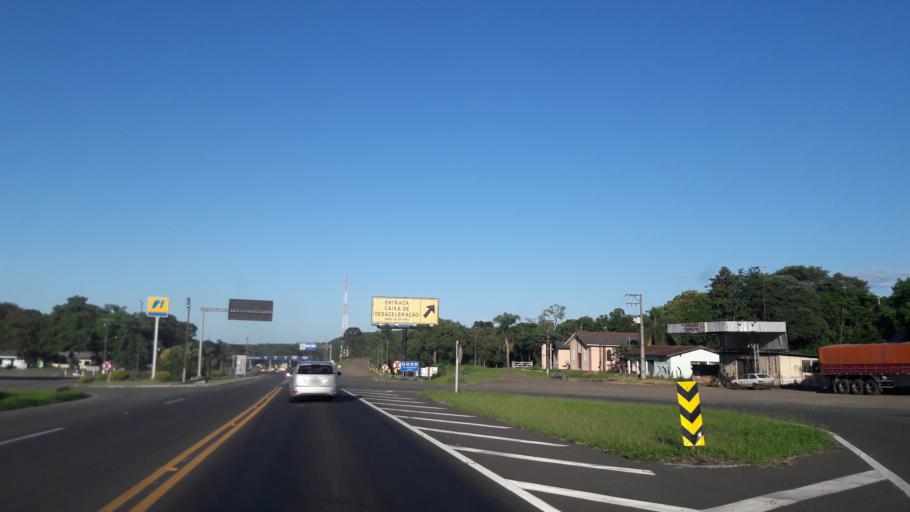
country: BR
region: Parana
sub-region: Prudentopolis
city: Prudentopolis
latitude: -25.3108
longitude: -51.1699
